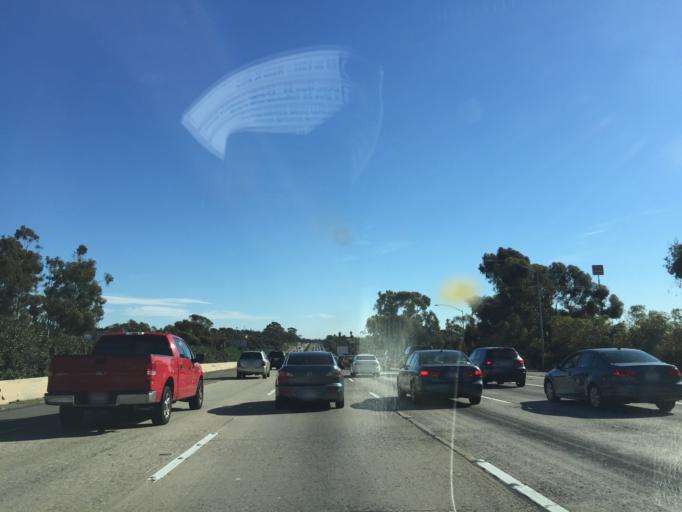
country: US
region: California
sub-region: San Diego County
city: Oceanside
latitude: 33.1935
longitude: -117.3651
